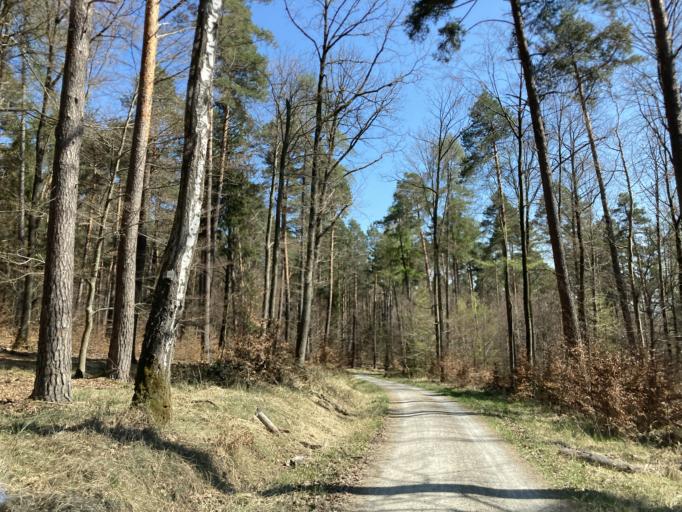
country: DE
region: Baden-Wuerttemberg
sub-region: Tuebingen Region
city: Tuebingen
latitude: 48.5699
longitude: 9.0164
